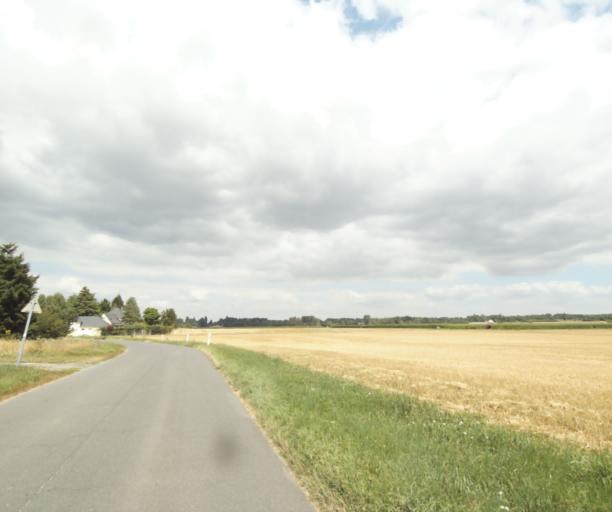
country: FR
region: Centre
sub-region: Departement du Loiret
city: Checy
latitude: 47.8816
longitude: 2.0383
